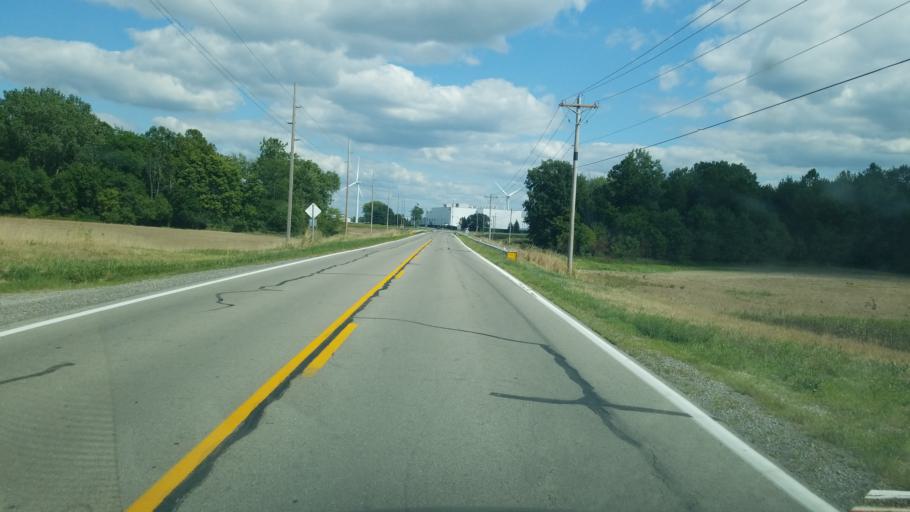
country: US
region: Ohio
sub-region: Logan County
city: Russells Point
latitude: 40.4519
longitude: -83.9093
